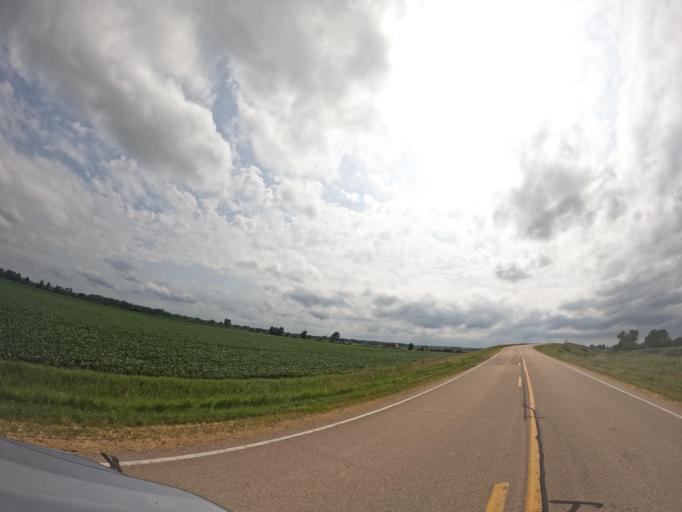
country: US
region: Iowa
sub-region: Clinton County
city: De Witt
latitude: 41.7858
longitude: -90.5644
